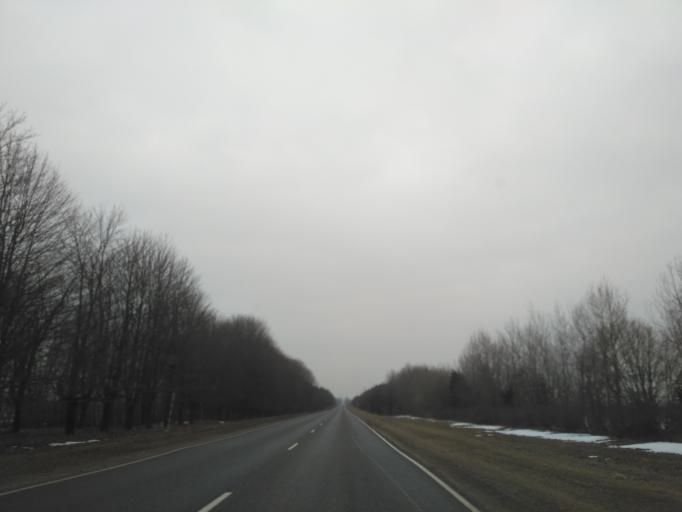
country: BY
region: Minsk
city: Haradzyeya
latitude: 53.3436
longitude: 26.4823
